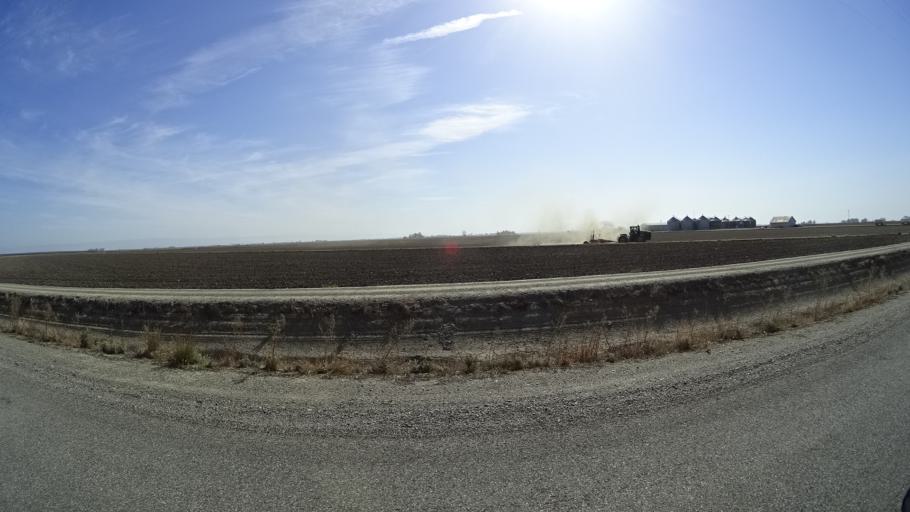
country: US
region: California
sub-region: Glenn County
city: Willows
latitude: 39.6012
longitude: -122.1170
